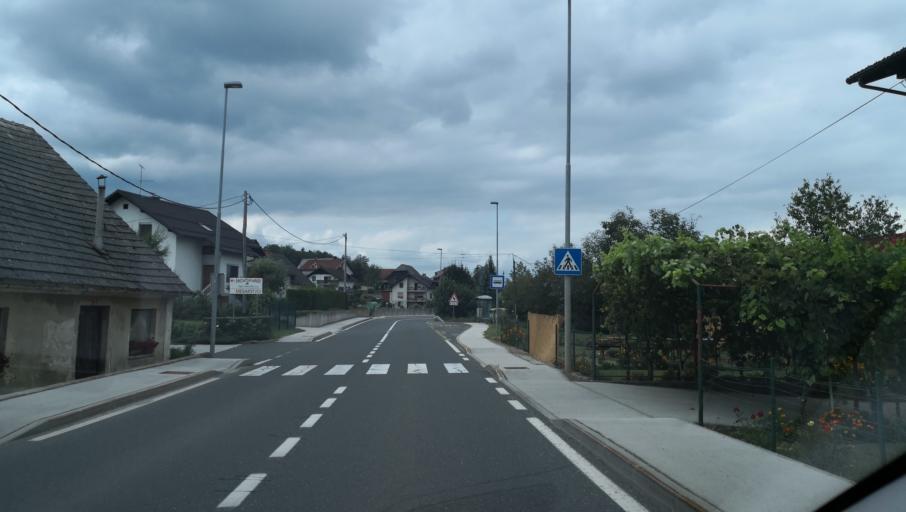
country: SI
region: Novo Mesto
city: Novo Mesto
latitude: 45.7675
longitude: 15.1958
